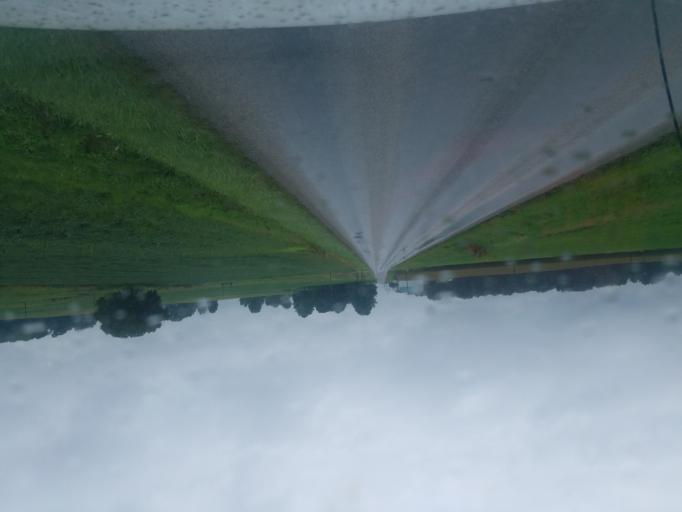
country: US
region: Ohio
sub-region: Wayne County
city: Creston
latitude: 40.9743
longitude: -81.9360
